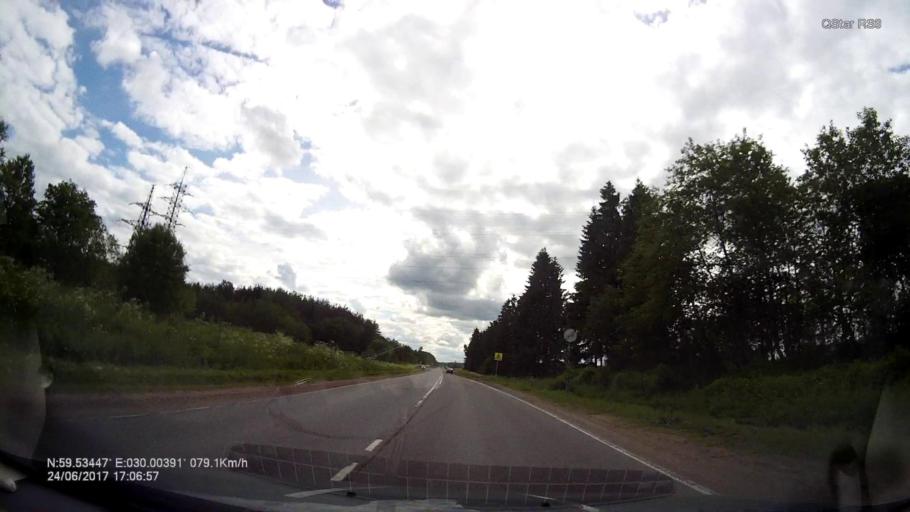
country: RU
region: Leningrad
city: Voyskovitsy
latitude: 59.5343
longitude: 30.0031
